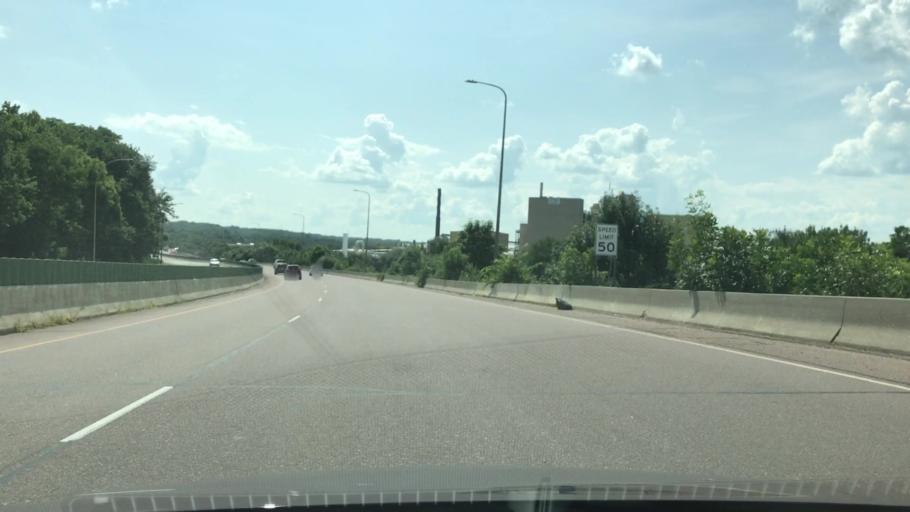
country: US
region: Minnesota
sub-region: Nicollet County
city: North Mankato
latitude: 44.1581
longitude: -94.0251
